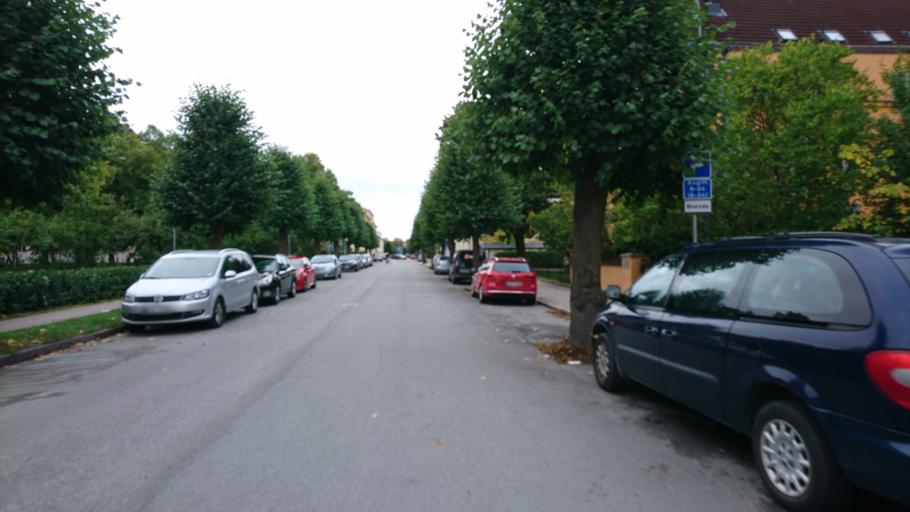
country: SE
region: Uppsala
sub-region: Uppsala Kommun
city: Uppsala
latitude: 59.8630
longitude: 17.6207
